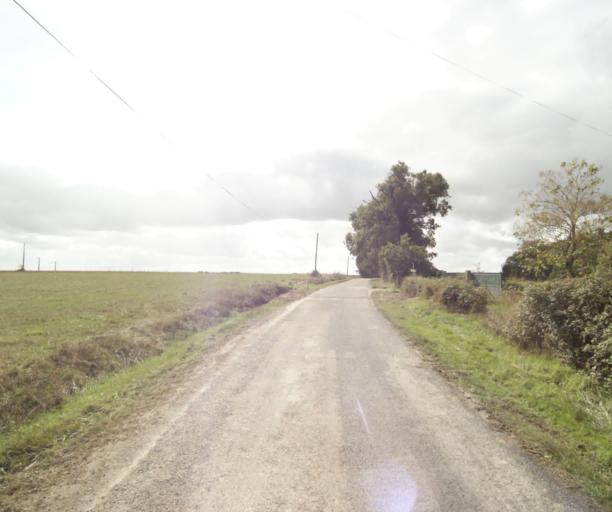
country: FR
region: Midi-Pyrenees
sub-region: Departement du Tarn-et-Garonne
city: Beaumont-de-Lomagne
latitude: 43.8667
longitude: 1.0679
